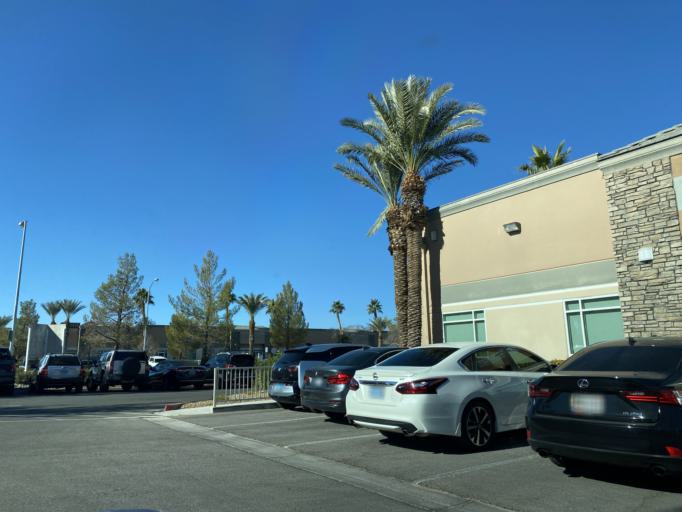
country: US
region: Nevada
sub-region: Clark County
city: Spring Valley
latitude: 36.0678
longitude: -115.2511
